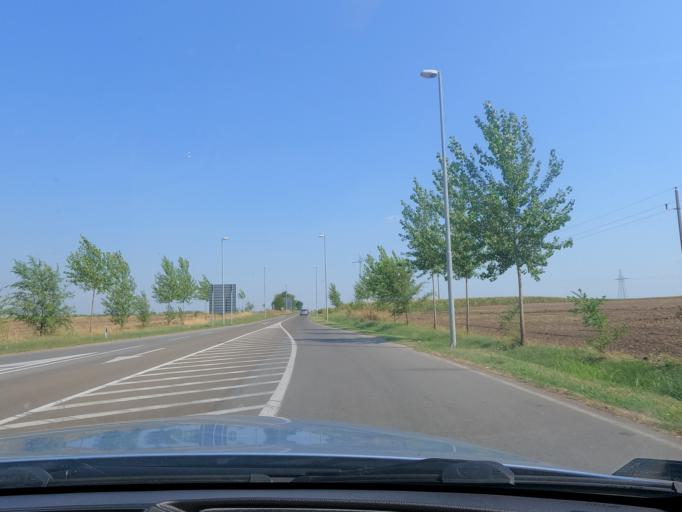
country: RS
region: Autonomna Pokrajina Vojvodina
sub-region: Severnobacki Okrug
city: Backa Topola
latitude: 45.7999
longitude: 19.6601
